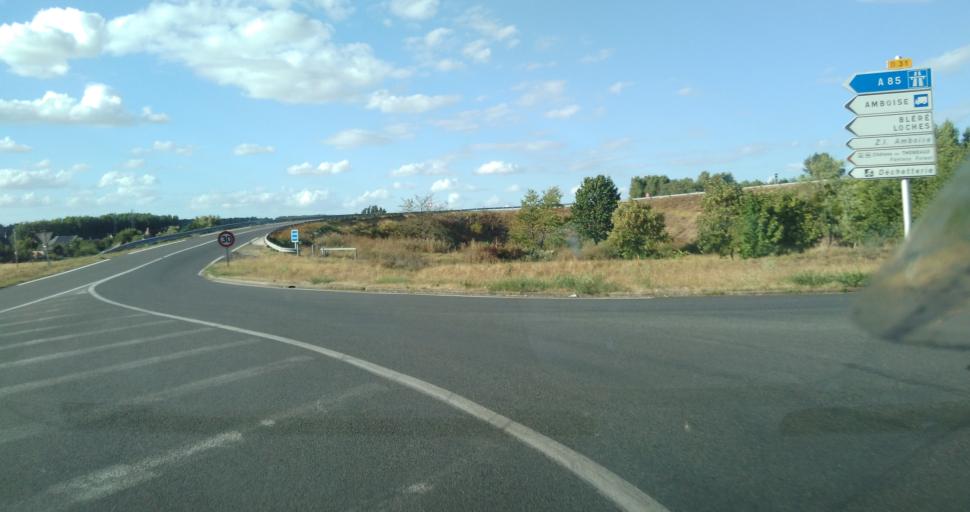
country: FR
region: Centre
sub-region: Departement d'Indre-et-Loire
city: Poce-sur-Cisse
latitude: 47.4301
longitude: 1.0063
